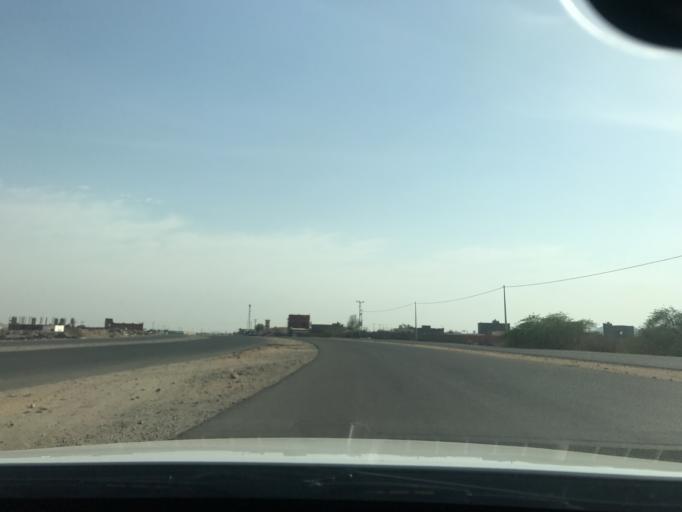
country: SA
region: Makkah
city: Al Jumum
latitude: 21.4508
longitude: 39.5226
